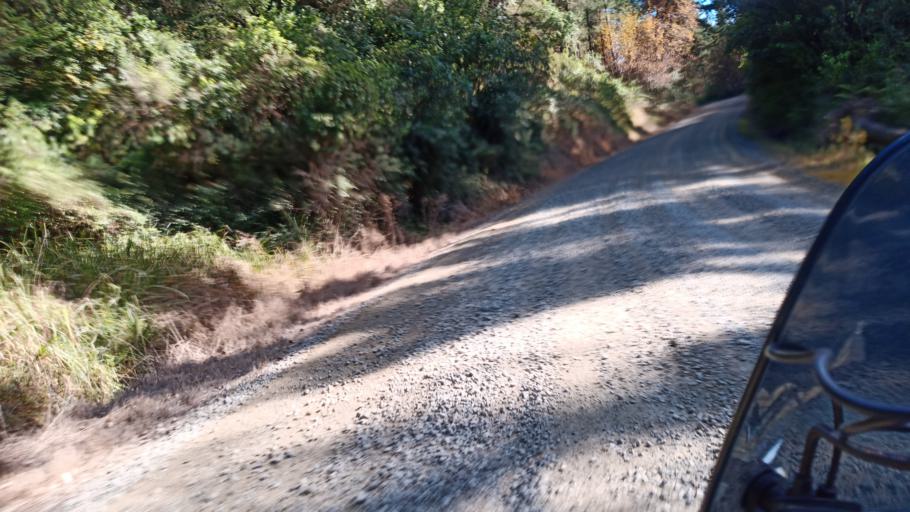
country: NZ
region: Hawke's Bay
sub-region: Wairoa District
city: Wairoa
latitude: -38.9295
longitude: 177.2184
